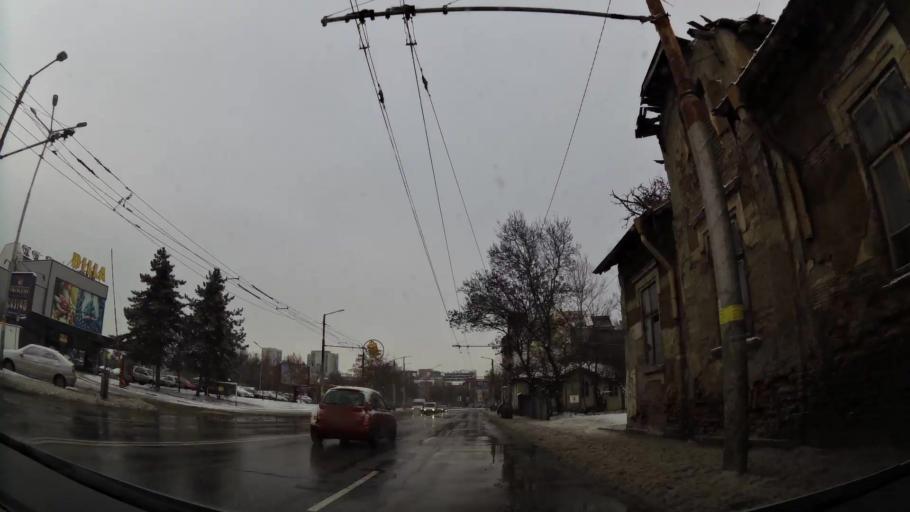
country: BG
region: Sofia-Capital
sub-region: Stolichna Obshtina
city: Sofia
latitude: 42.7037
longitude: 23.3113
